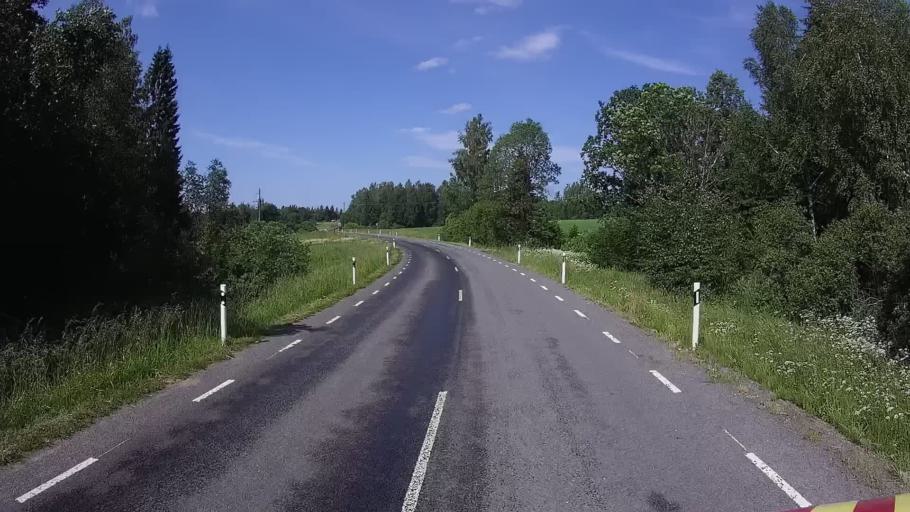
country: EE
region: Viljandimaa
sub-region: Karksi vald
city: Karksi-Nuia
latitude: 58.0873
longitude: 25.5583
